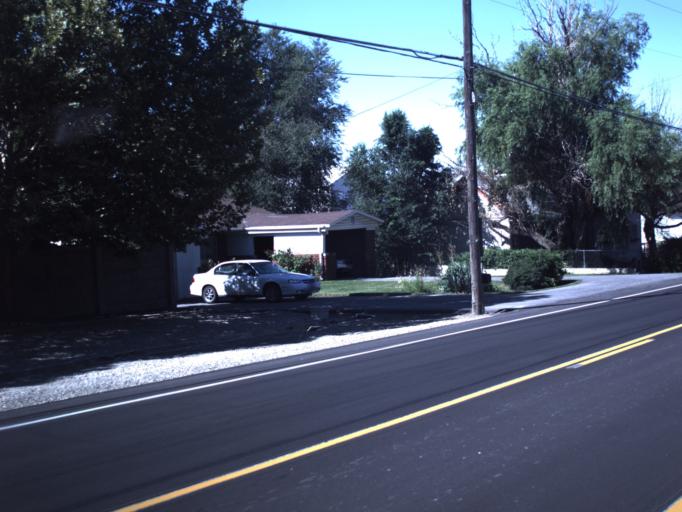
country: US
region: Utah
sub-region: Salt Lake County
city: Holladay
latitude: 40.6743
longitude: -111.8366
